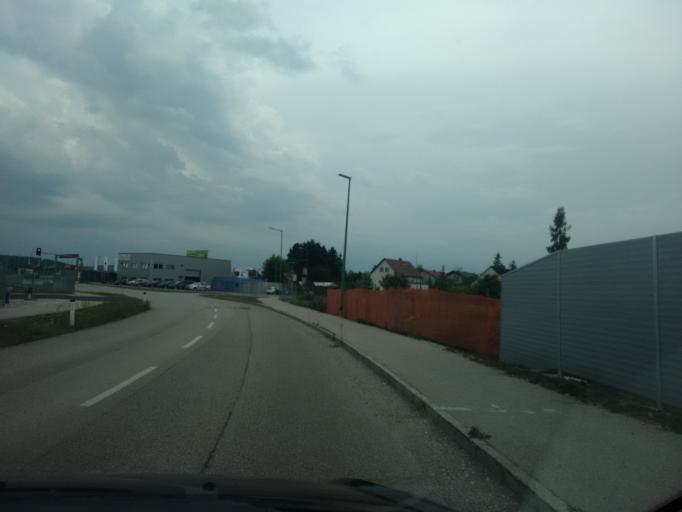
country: AT
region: Upper Austria
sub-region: Wels Stadt
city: Wels
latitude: 48.1845
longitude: 14.0713
